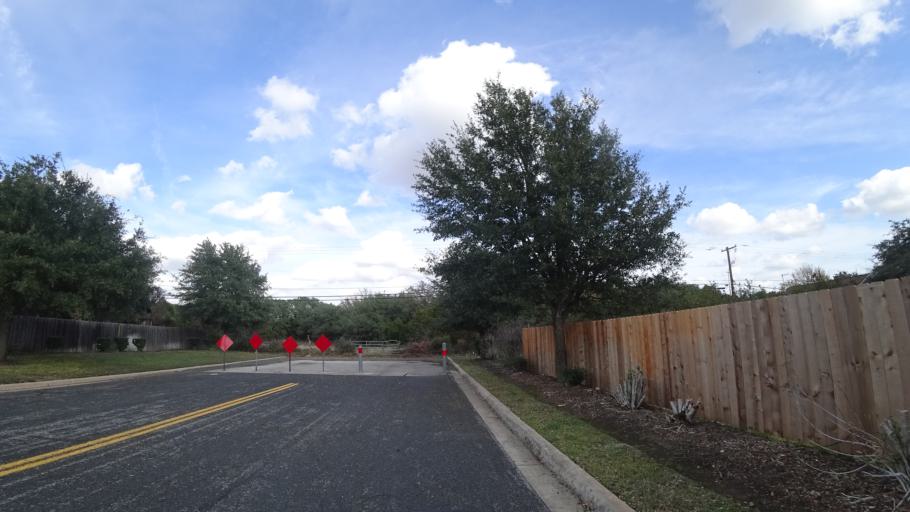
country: US
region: Texas
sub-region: Williamson County
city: Brushy Creek
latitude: 30.5112
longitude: -97.7210
